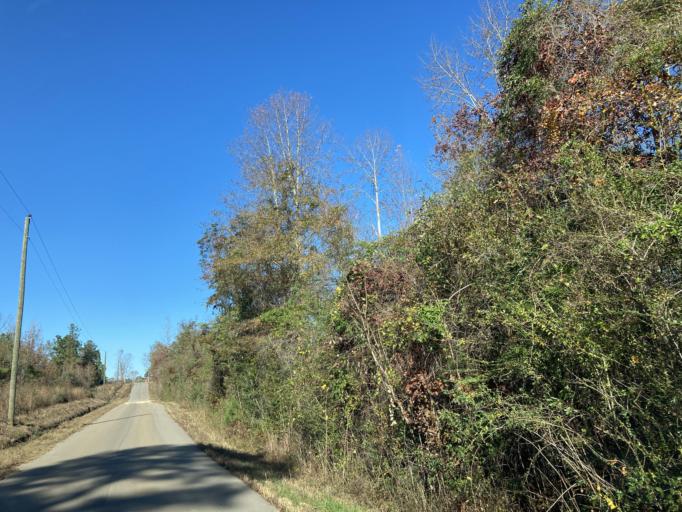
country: US
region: Mississippi
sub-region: Lamar County
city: Sumrall
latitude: 31.3327
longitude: -89.6226
